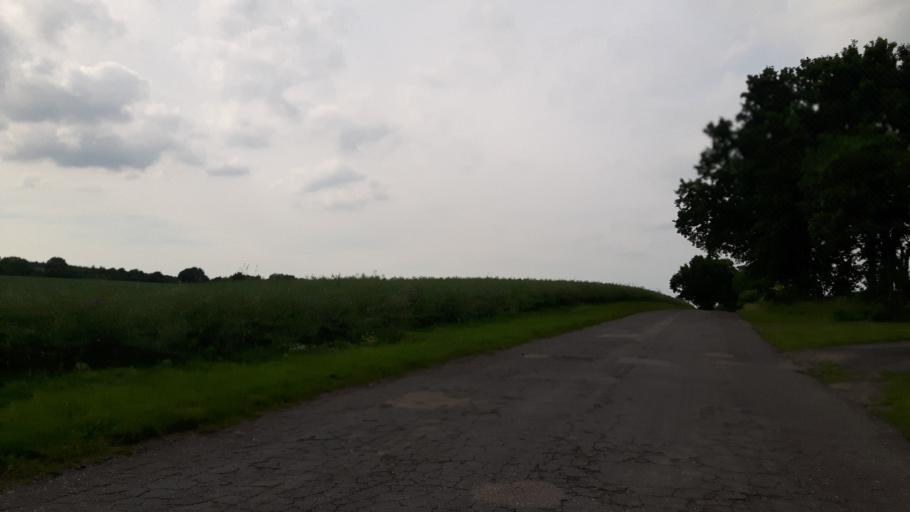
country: PL
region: West Pomeranian Voivodeship
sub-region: Powiat gryficki
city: Gryfice
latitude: 53.8417
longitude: 15.1607
